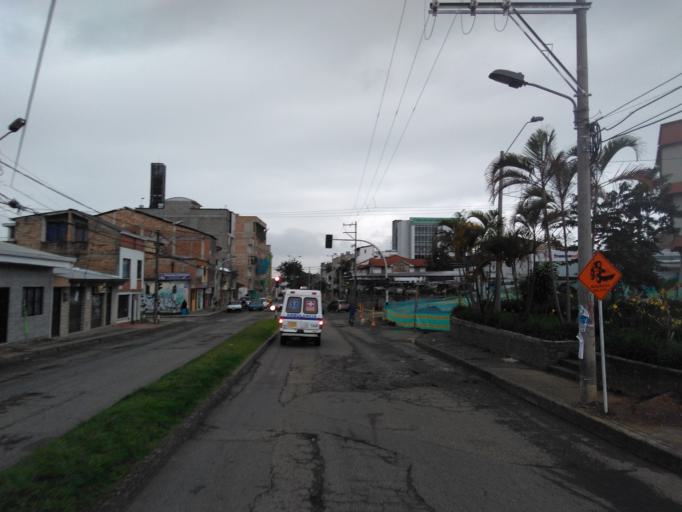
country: CO
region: Cauca
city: Popayan
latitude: 2.4524
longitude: -76.5970
